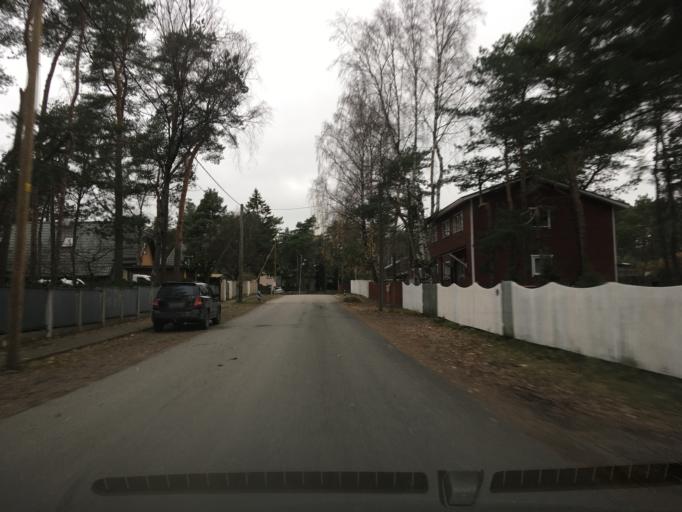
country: EE
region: Harju
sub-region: Tallinna linn
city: Tallinn
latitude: 59.3789
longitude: 24.7082
